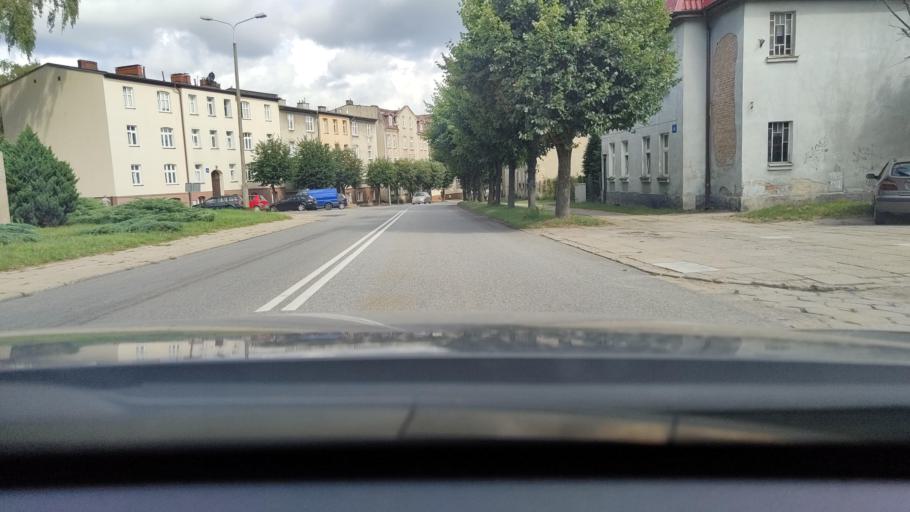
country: PL
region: Pomeranian Voivodeship
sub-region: Powiat wejherowski
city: Wejherowo
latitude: 54.5975
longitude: 18.2322
